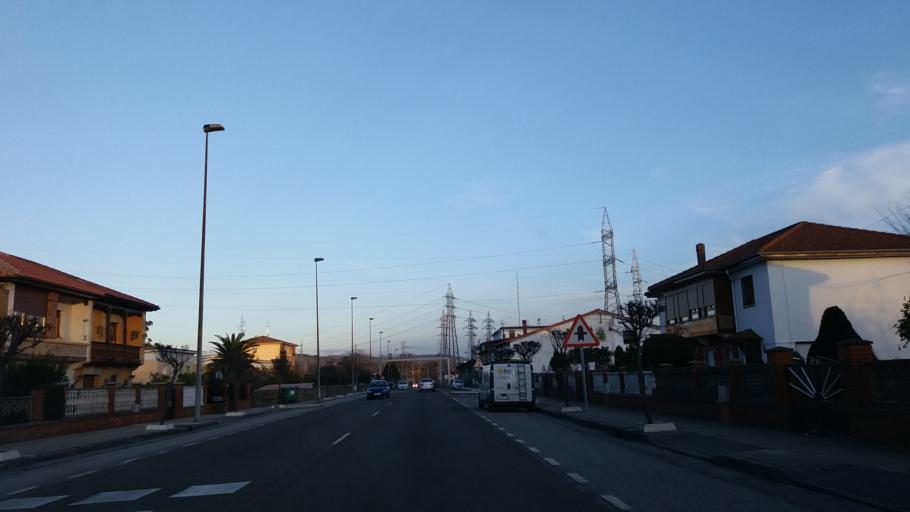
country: ES
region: Cantabria
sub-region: Provincia de Cantabria
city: Reocin
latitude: 43.3577
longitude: -4.0805
